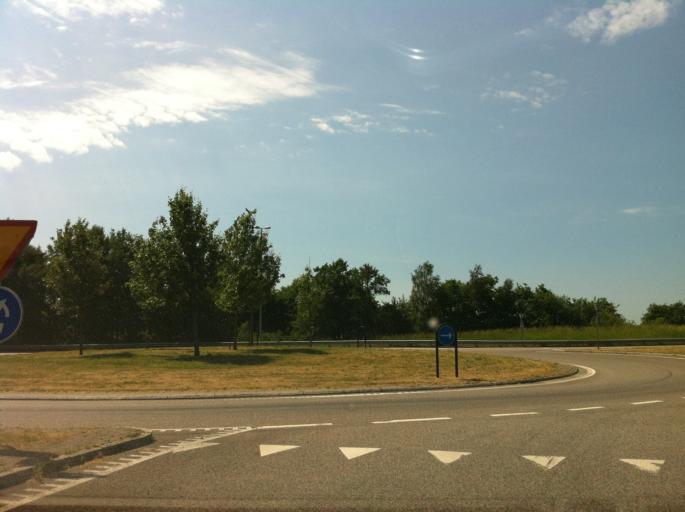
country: SE
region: Skane
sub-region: Helsingborg
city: Hyllinge
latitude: 56.0971
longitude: 12.8590
